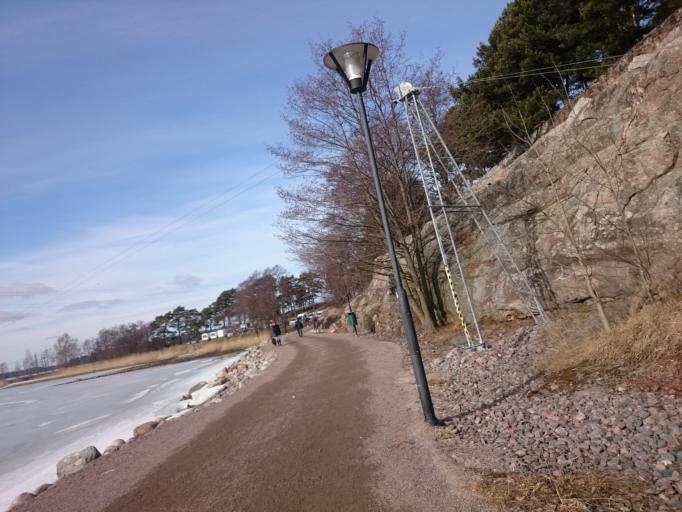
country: FI
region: Uusimaa
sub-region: Helsinki
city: Helsinki
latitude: 60.1711
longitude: 24.9056
